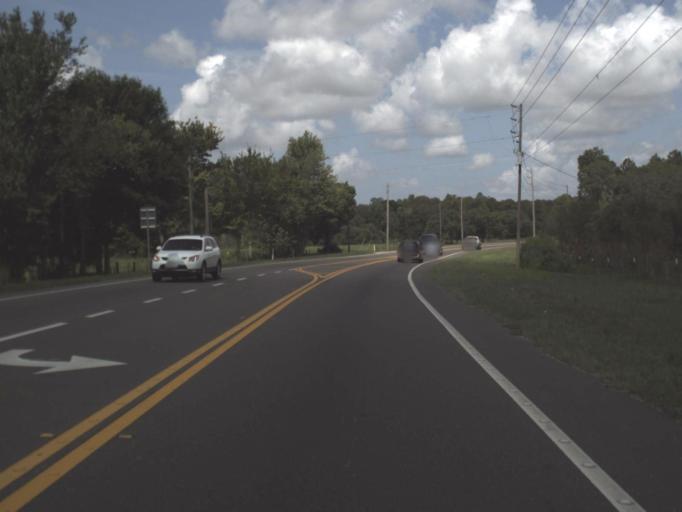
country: US
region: Florida
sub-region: Pasco County
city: Shady Hills
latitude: 28.3245
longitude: -82.5223
